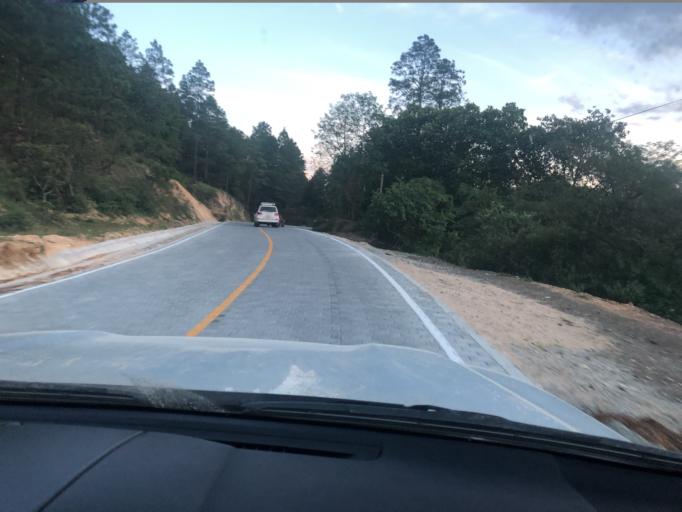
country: NI
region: Nueva Segovia
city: Ocotal
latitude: 13.6745
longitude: -86.6167
